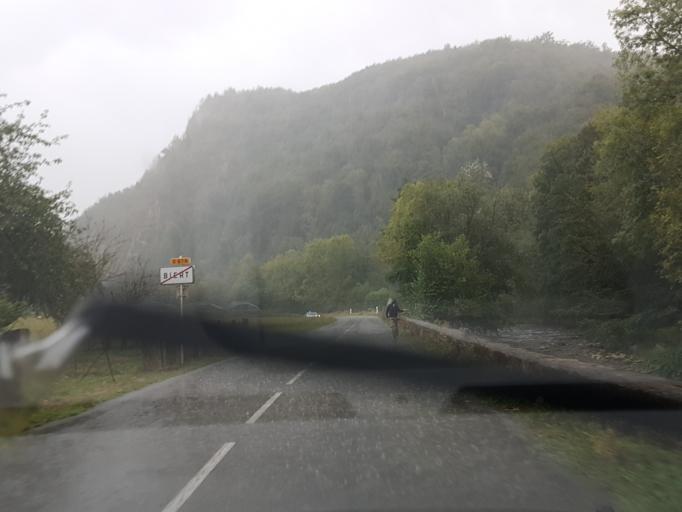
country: FR
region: Midi-Pyrenees
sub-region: Departement de l'Ariege
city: Saint-Girons
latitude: 42.8977
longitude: 1.3177
